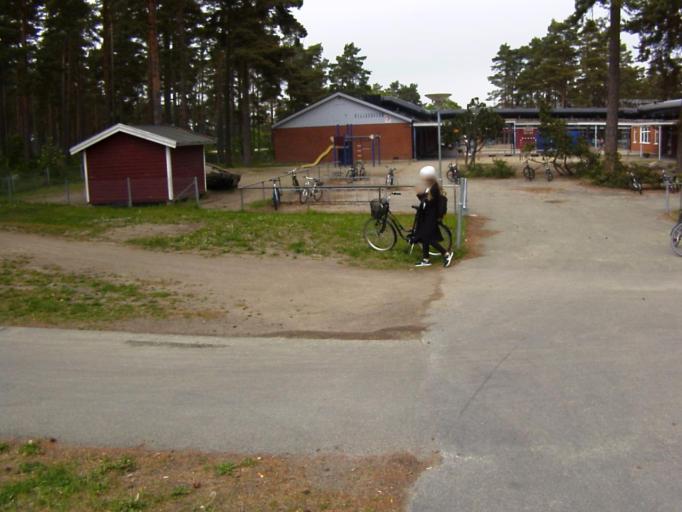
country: SE
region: Skane
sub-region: Kristianstads Kommun
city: Ahus
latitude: 55.9413
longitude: 14.2825
